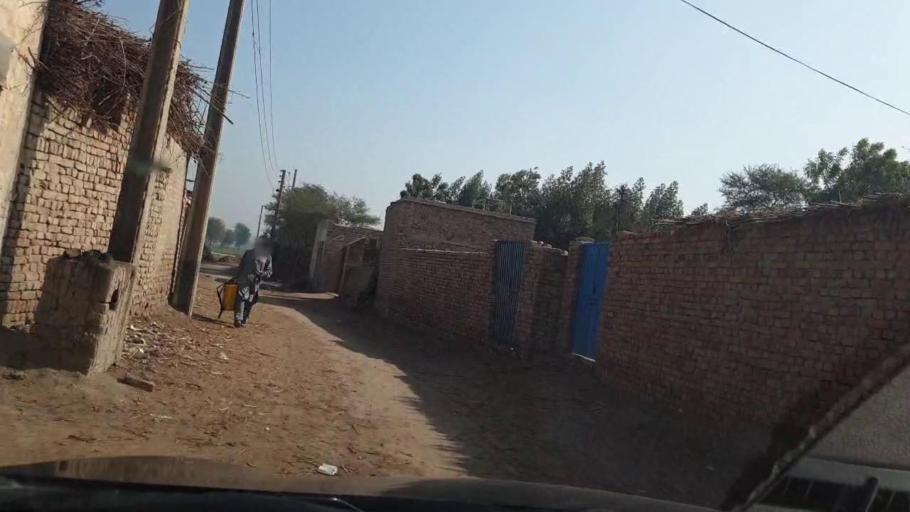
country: PK
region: Sindh
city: Ubauro
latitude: 28.1128
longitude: 69.7430
